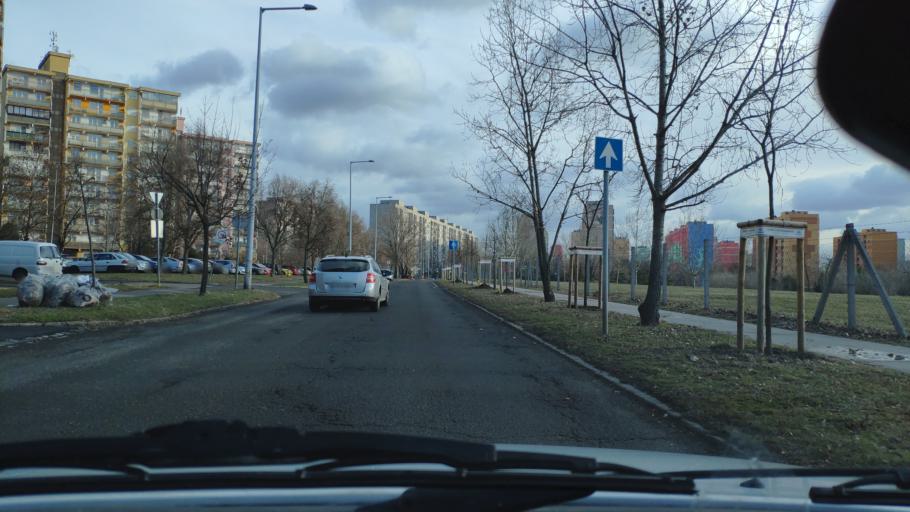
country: HU
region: Budapest
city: Budapest X. keruelet
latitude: 47.4747
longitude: 19.1585
